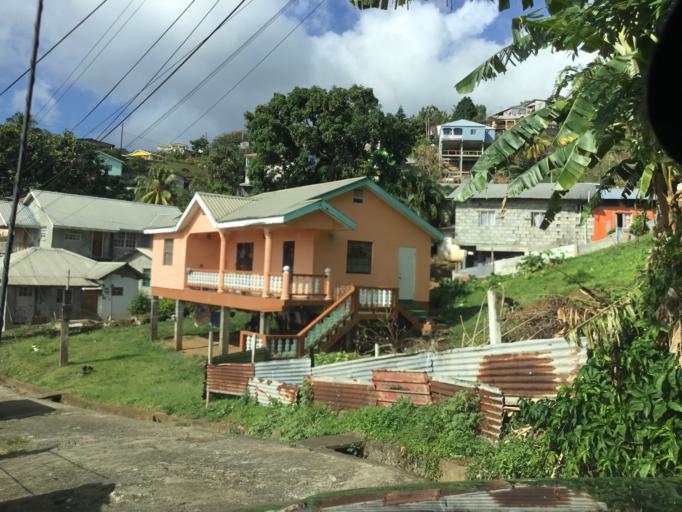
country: VC
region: Saint George
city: Kingstown
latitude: 13.1668
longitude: -61.2177
